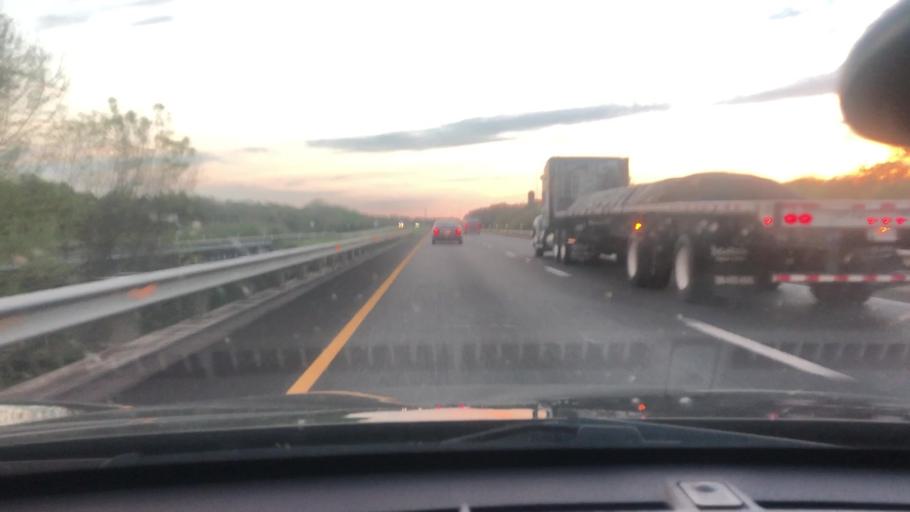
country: US
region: Texas
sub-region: Victoria County
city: Inez
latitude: 28.9130
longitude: -96.7743
